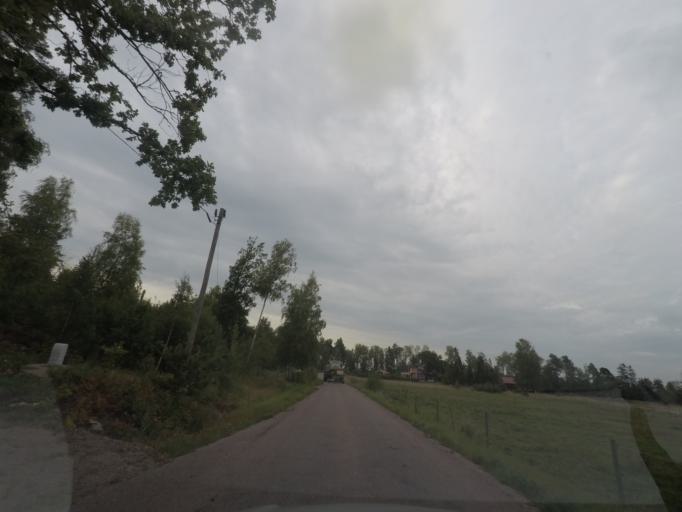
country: SE
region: Vaestmanland
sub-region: Hallstahammars Kommun
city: Kolback
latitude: 59.5014
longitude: 16.1906
